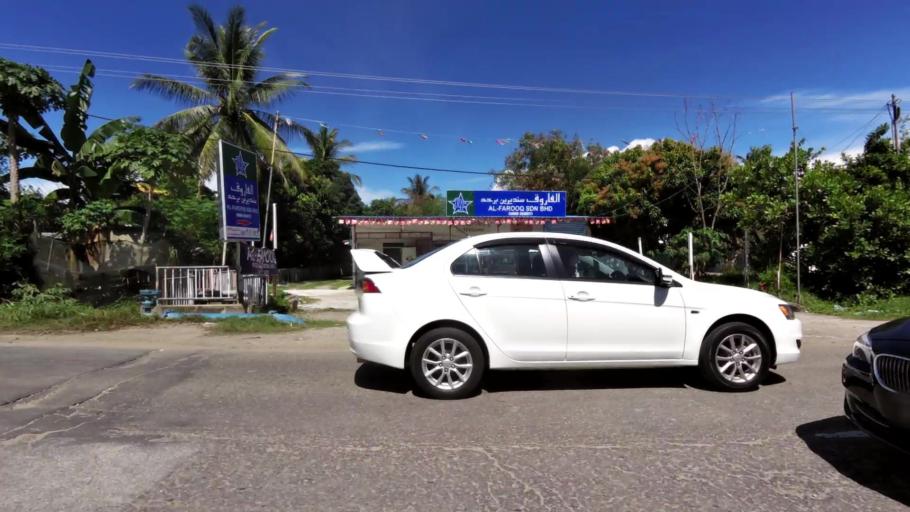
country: BN
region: Brunei and Muara
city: Bandar Seri Begawan
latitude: 5.0203
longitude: 115.0578
